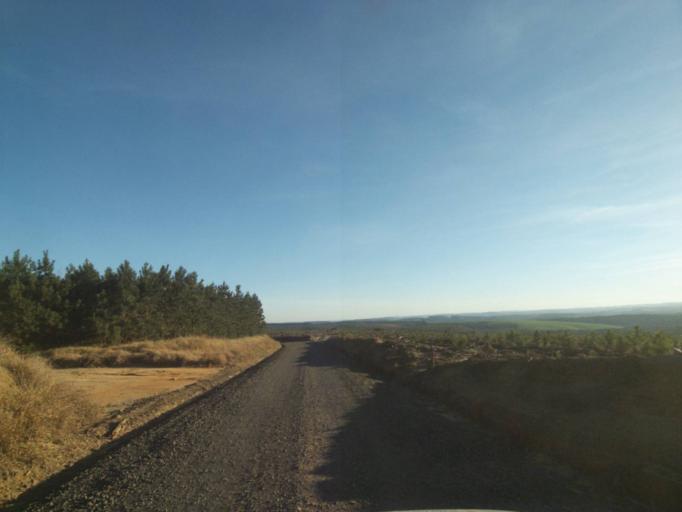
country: BR
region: Parana
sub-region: Telemaco Borba
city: Telemaco Borba
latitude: -24.4541
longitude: -50.6009
